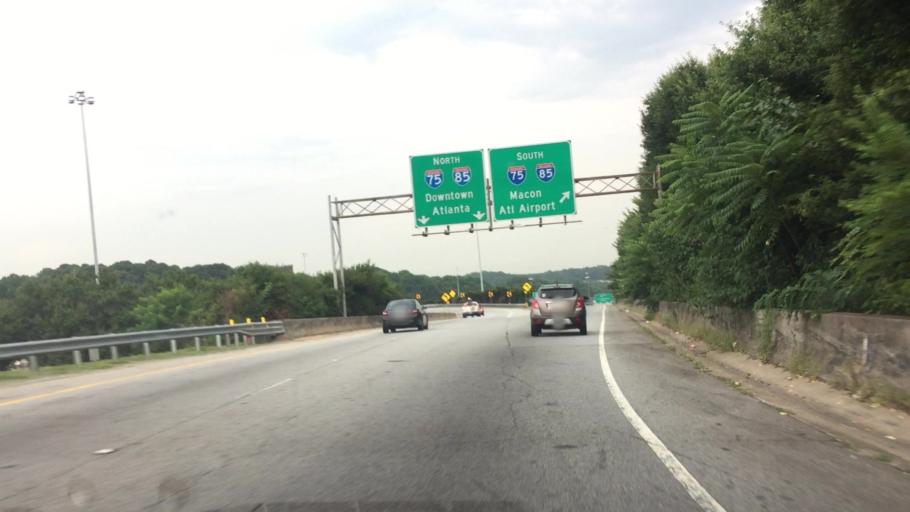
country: US
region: Georgia
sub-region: Fulton County
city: East Point
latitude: 33.6961
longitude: -84.4074
